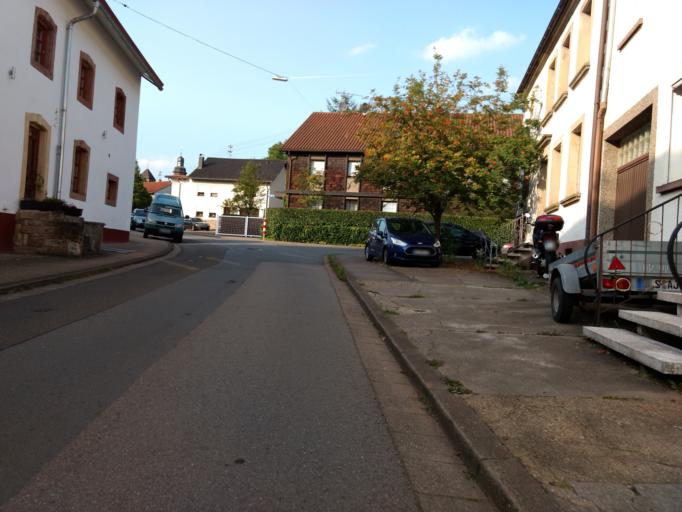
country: DE
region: Saarland
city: Rehlingen-Siersburg
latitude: 49.3554
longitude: 6.6680
